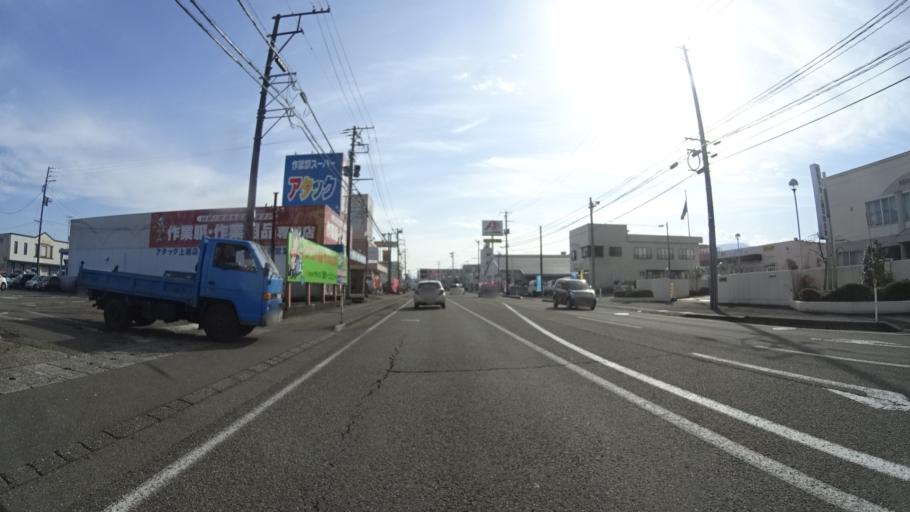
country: JP
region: Niigata
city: Joetsu
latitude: 37.1381
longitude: 138.2411
